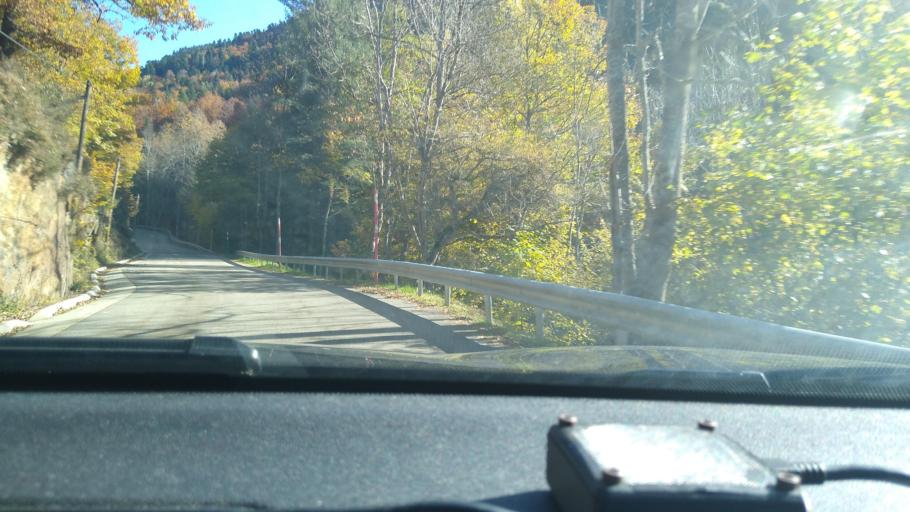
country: FR
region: Midi-Pyrenees
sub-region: Departement de l'Ariege
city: Ax-les-Thermes
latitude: 42.7193
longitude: 1.9072
